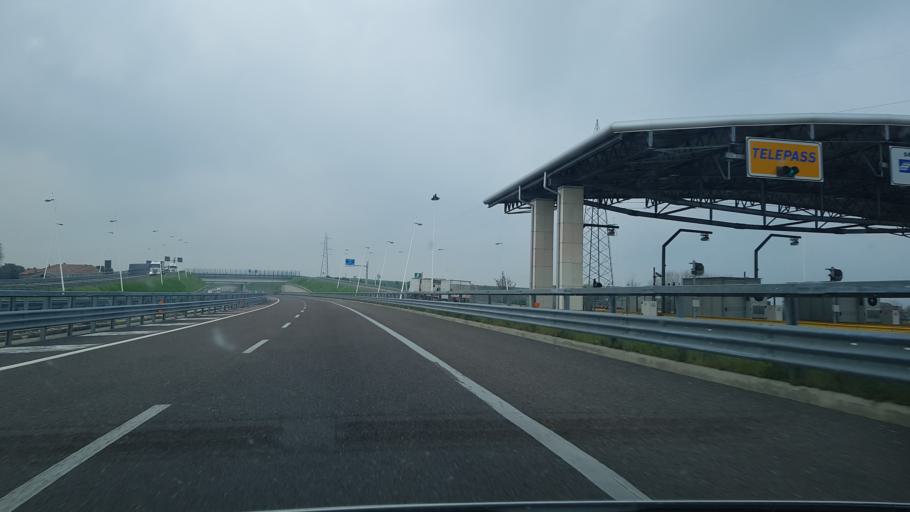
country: IT
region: Veneto
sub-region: Provincia di Vicenza
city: Villaganzerla
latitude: 45.4571
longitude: 11.6286
